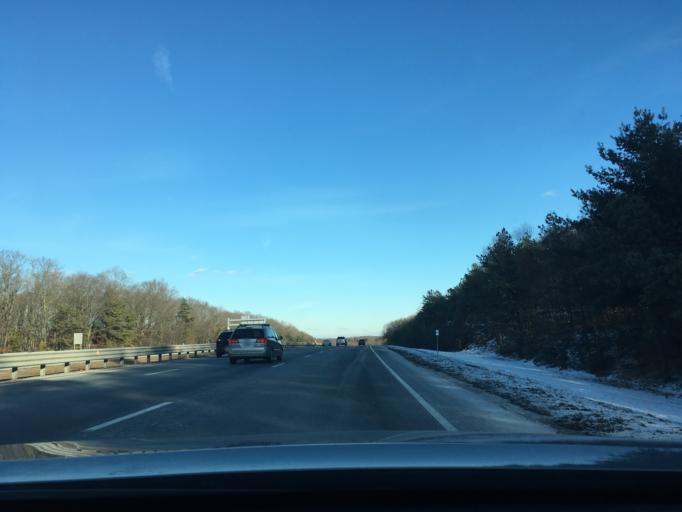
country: US
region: Rhode Island
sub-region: Kent County
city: West Warwick
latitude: 41.6592
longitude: -71.5452
